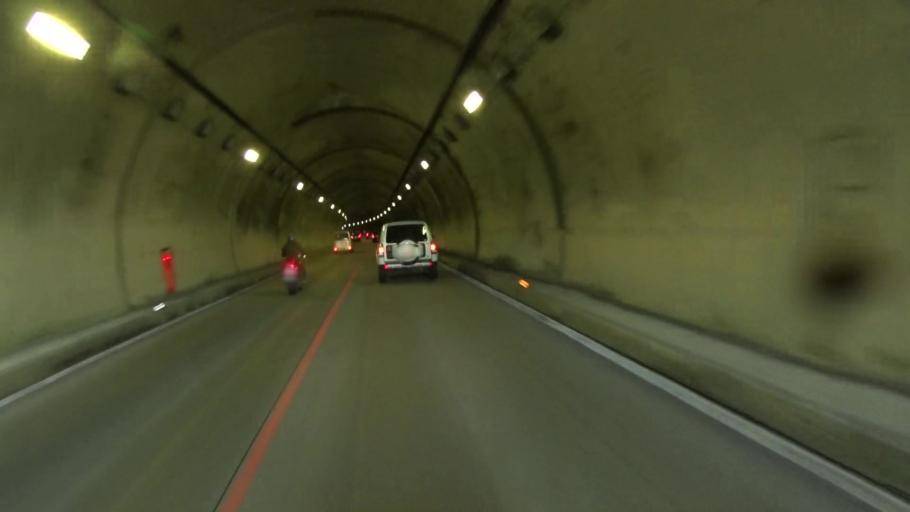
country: JP
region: Kyoto
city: Kameoka
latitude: 34.9983
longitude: 135.5736
